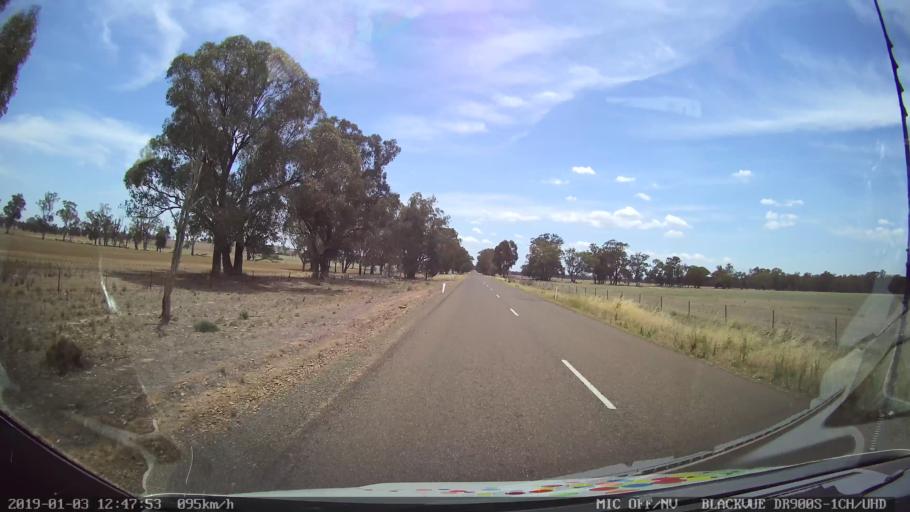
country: AU
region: New South Wales
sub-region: Weddin
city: Grenfell
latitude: -33.7213
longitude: 148.2458
